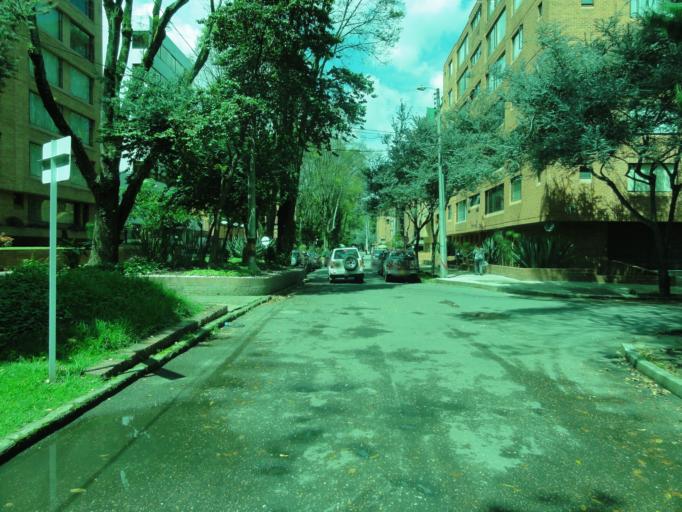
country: CO
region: Bogota D.C.
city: Barrio San Luis
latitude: 4.6740
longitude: -74.0506
